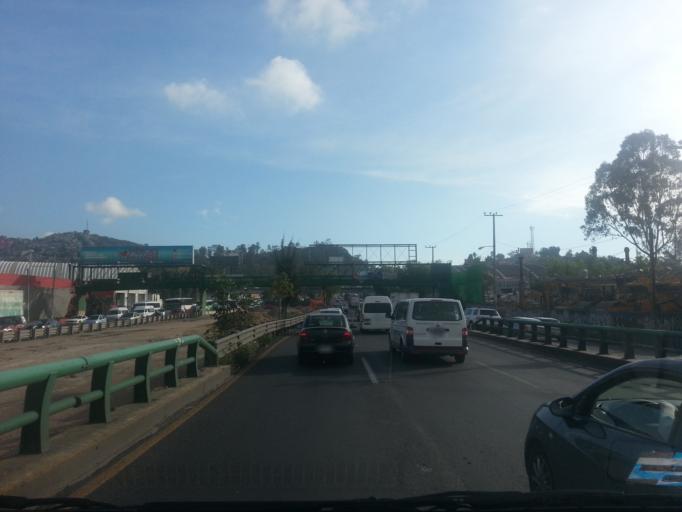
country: MX
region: Mexico City
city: Gustavo A. Madero
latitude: 19.5171
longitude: -99.0994
